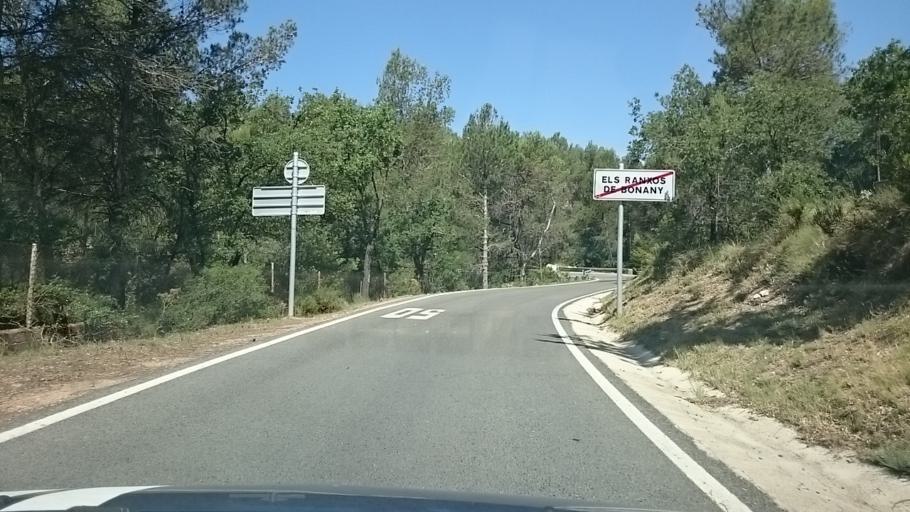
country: ES
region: Catalonia
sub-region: Provincia de Tarragona
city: Querol
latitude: 41.3968
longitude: 1.4536
